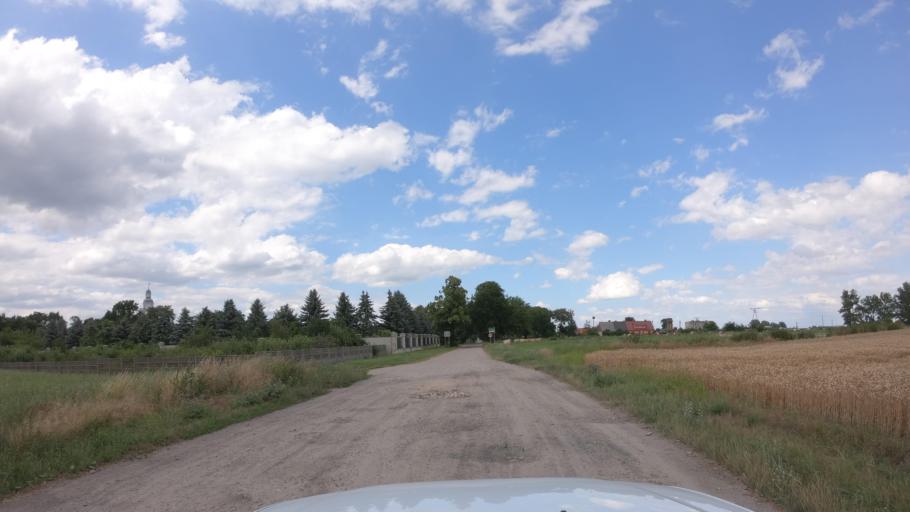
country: PL
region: West Pomeranian Voivodeship
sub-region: Powiat pyrzycki
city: Warnice
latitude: 53.2661
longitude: 14.9090
